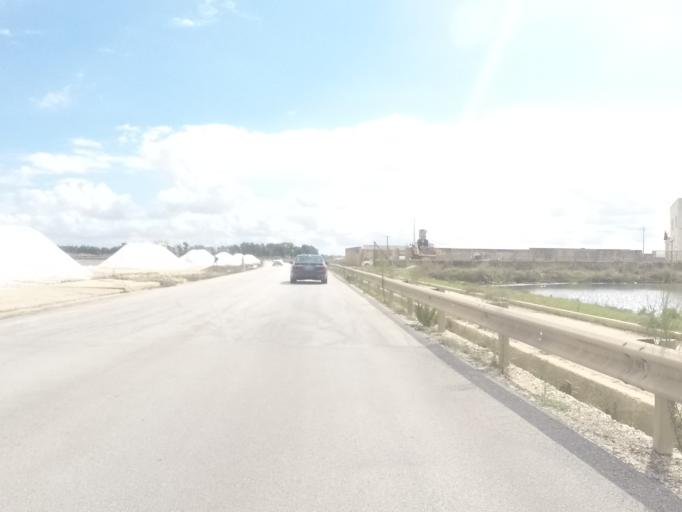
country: IT
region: Sicily
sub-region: Trapani
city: Trapani
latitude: 37.9946
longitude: 12.5348
